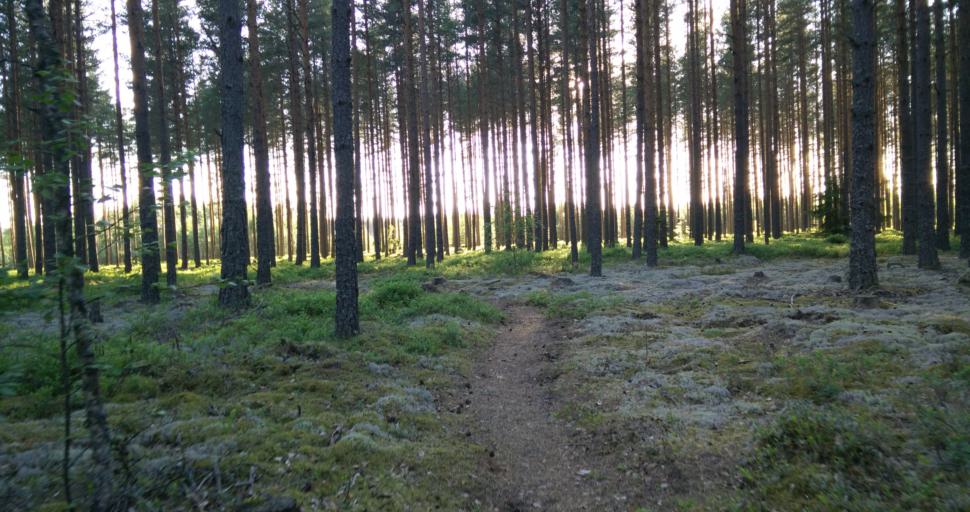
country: SE
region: Vaermland
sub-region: Hagfors Kommun
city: Hagfors
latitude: 60.0173
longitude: 13.5852
